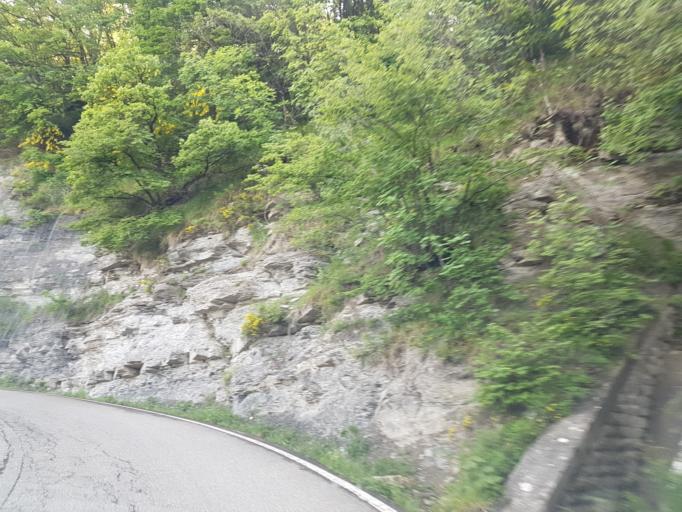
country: IT
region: Emilia-Romagna
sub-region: Forli-Cesena
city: San Piero in Bagno
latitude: 43.8119
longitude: 11.9351
